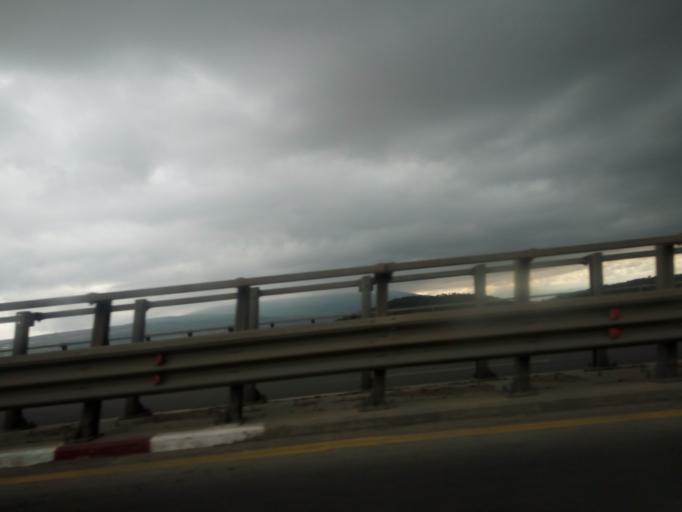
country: DZ
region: Bordj Bou Arreridj
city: El Achir
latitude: 36.0933
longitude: 4.5821
